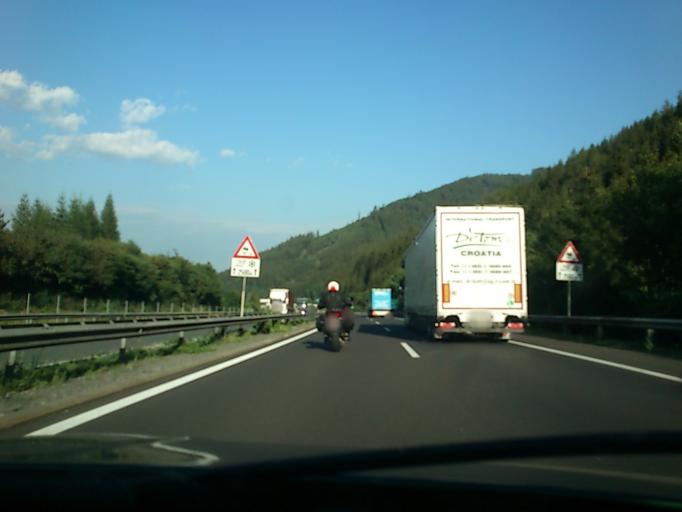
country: AT
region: Styria
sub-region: Politischer Bezirk Leoben
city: Kammern im Liesingtal
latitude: 47.3873
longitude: 14.8886
